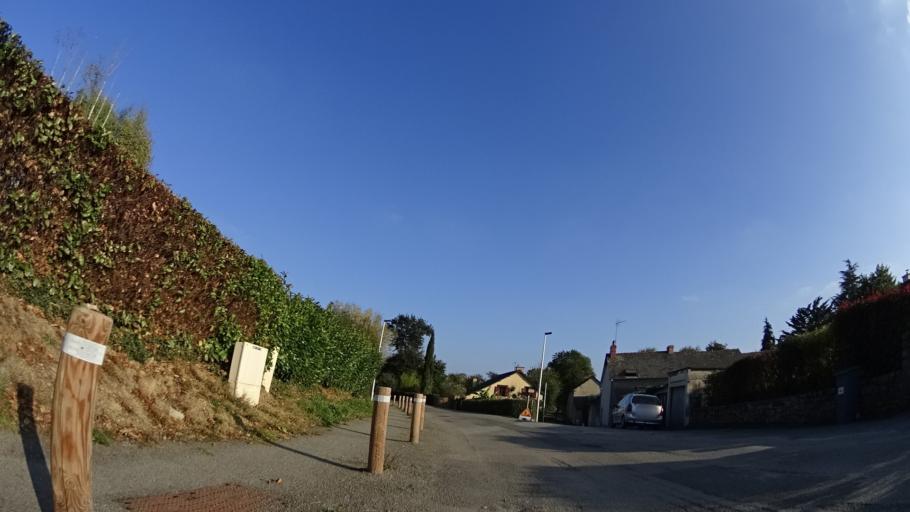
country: FR
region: Brittany
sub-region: Departement d'Ille-et-Vilaine
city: Geveze
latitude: 48.2215
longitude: -1.7822
